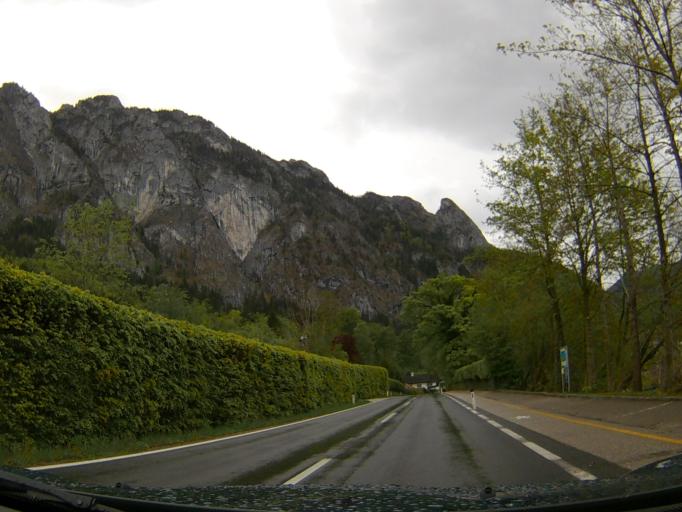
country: AT
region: Upper Austria
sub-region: Politischer Bezirk Vocklabruck
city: Steinbach am Attersee
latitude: 47.8129
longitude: 13.5467
